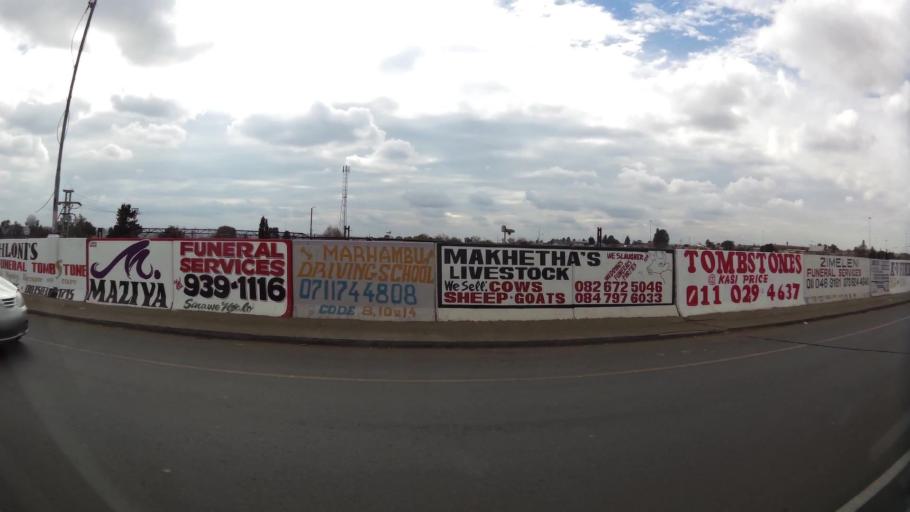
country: ZA
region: Gauteng
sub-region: City of Johannesburg Metropolitan Municipality
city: Soweto
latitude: -26.2744
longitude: 27.8875
